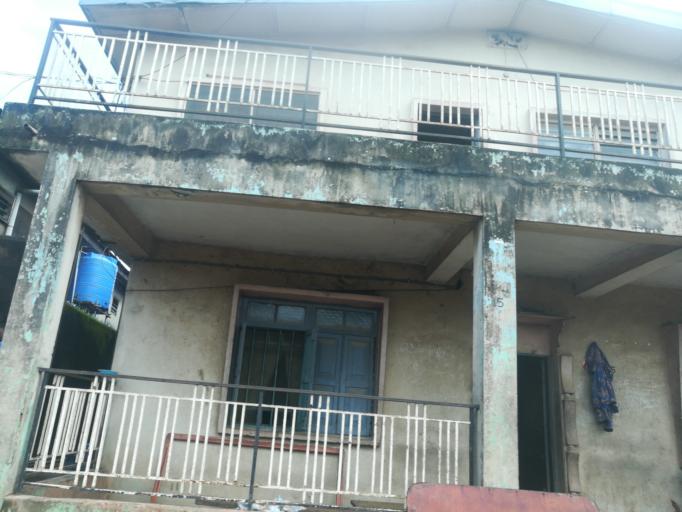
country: NG
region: Lagos
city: Agege
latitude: 6.6162
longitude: 3.3307
